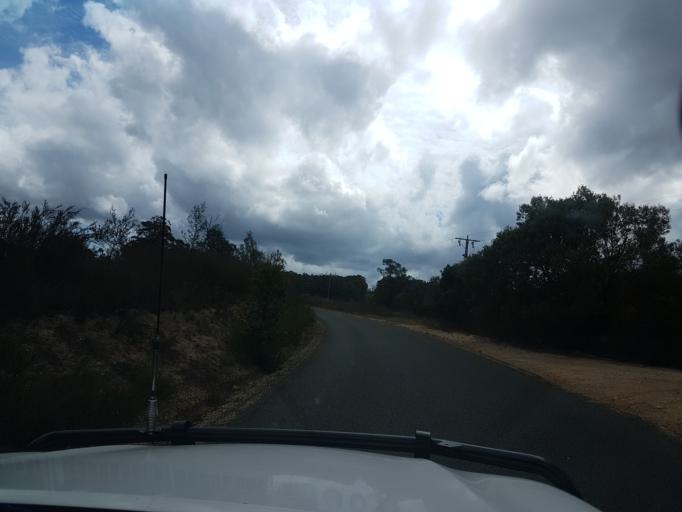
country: AU
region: Victoria
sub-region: East Gippsland
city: Bairnsdale
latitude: -37.6767
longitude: 147.5512
